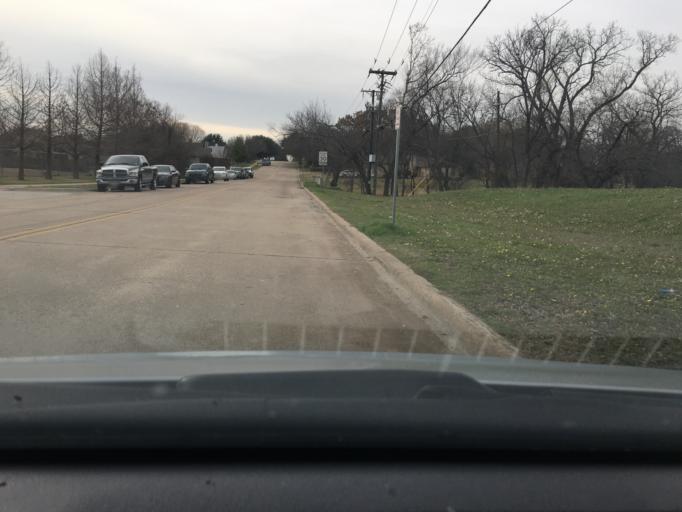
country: US
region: Texas
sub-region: Collin County
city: McKinney
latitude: 33.1944
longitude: -96.6405
